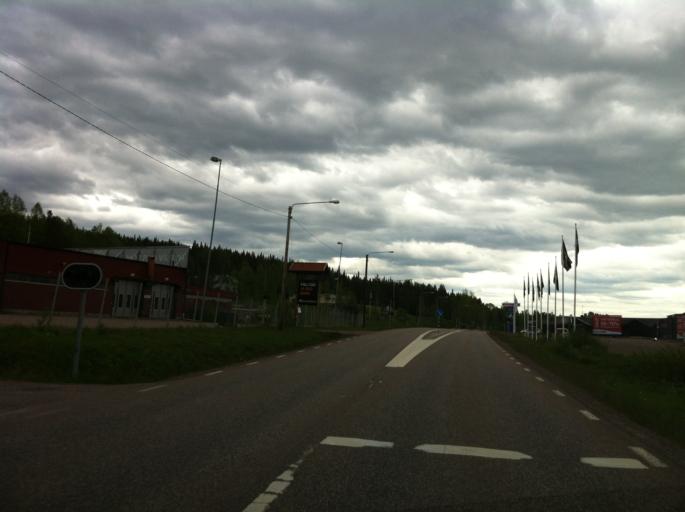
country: SE
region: Dalarna
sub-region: Malung-Saelens kommun
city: Malung
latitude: 61.1367
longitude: 13.2806
